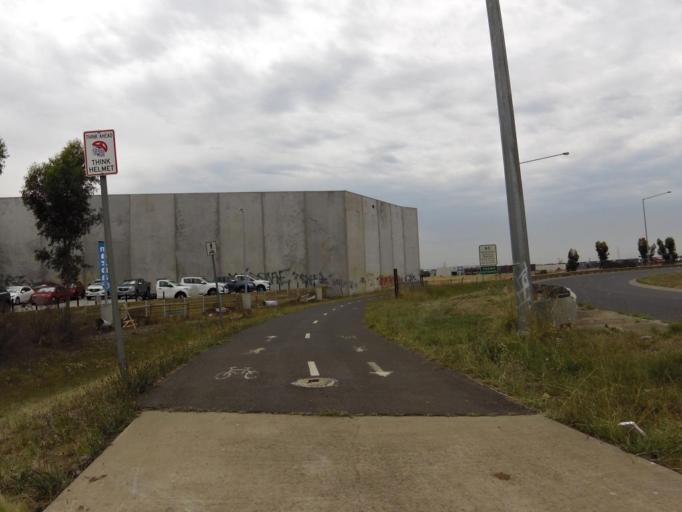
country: AU
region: Victoria
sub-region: Melton
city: Caroline Springs
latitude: -37.7591
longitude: 144.7398
